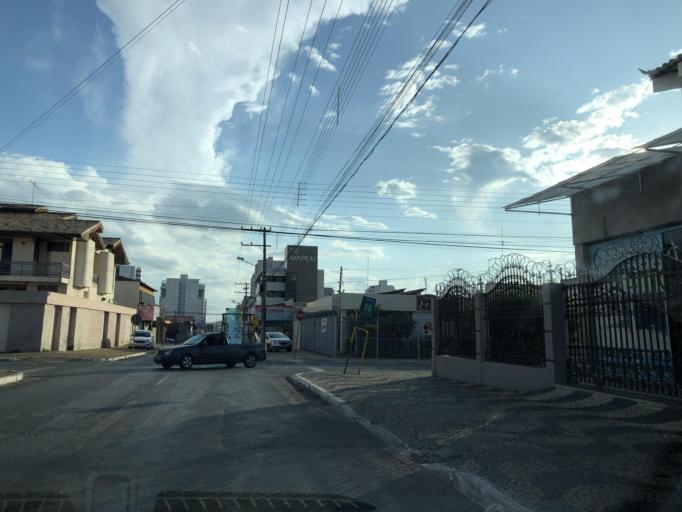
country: BR
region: Federal District
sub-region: Brasilia
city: Brasilia
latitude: -15.8288
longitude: -48.0553
